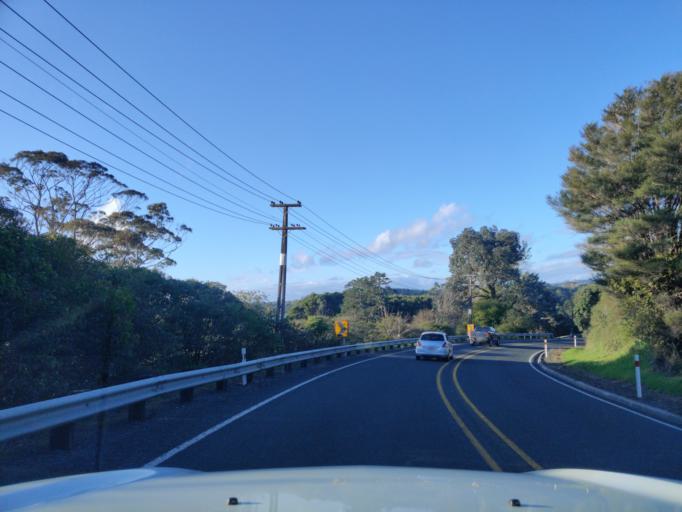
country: NZ
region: Auckland
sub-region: Auckland
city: Pakuranga
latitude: -36.9436
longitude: 174.9611
